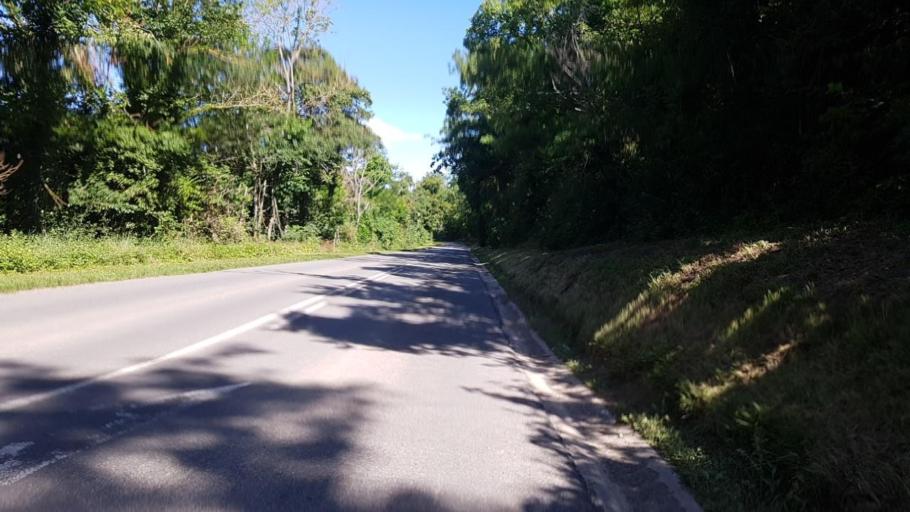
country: FR
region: Picardie
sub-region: Departement de l'Aisne
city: Charly-sur-Marne
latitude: 48.9737
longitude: 3.2528
